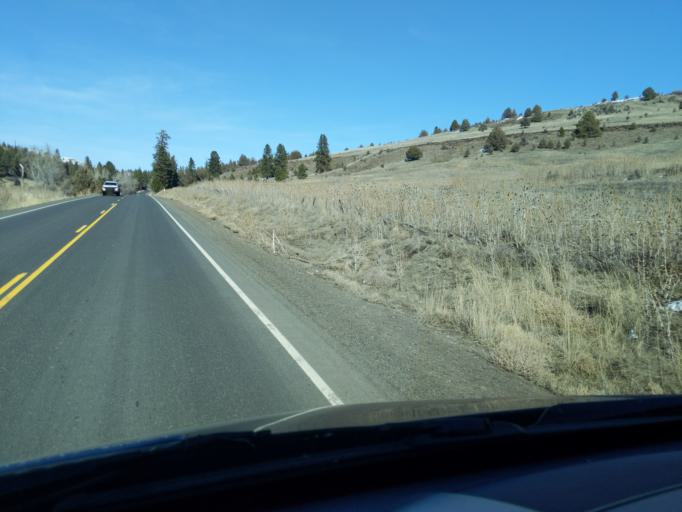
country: US
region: Oregon
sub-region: Grant County
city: John Day
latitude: 44.8575
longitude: -119.0284
